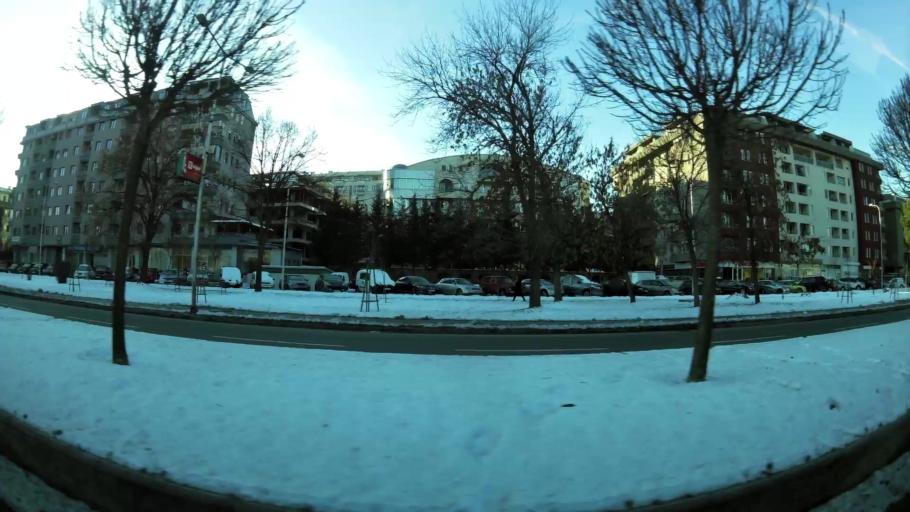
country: MK
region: Karpos
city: Skopje
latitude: 42.0069
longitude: 21.4089
